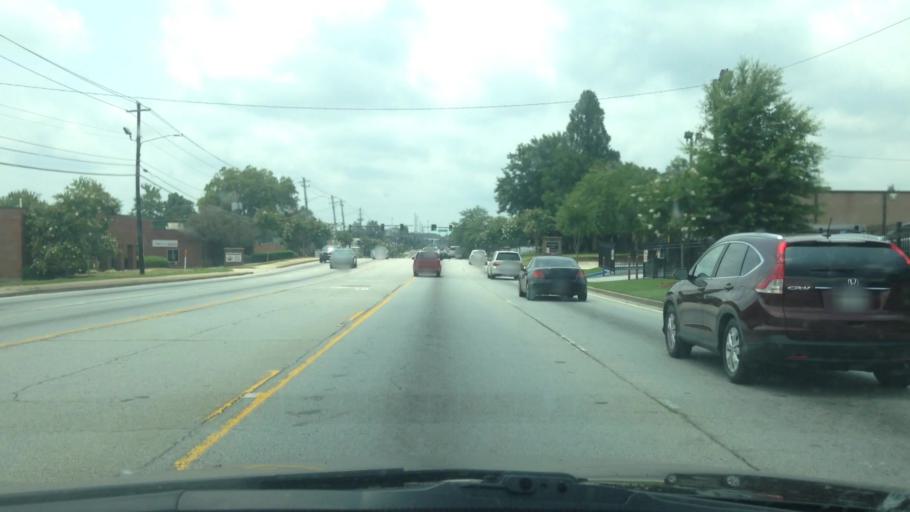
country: US
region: Georgia
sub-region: DeKalb County
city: Tucker
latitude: 33.8471
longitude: -84.2010
